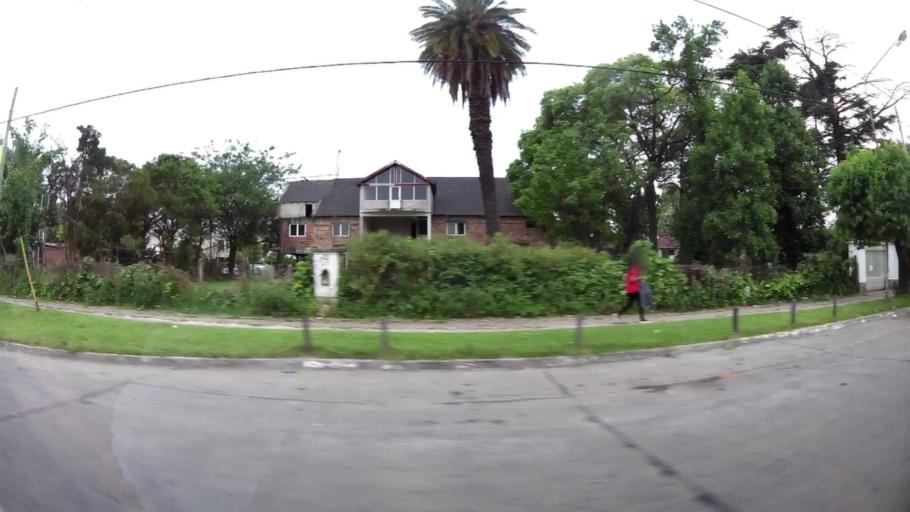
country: AR
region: Buenos Aires
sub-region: Partido de Moron
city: Moron
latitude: -34.6624
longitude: -58.5964
